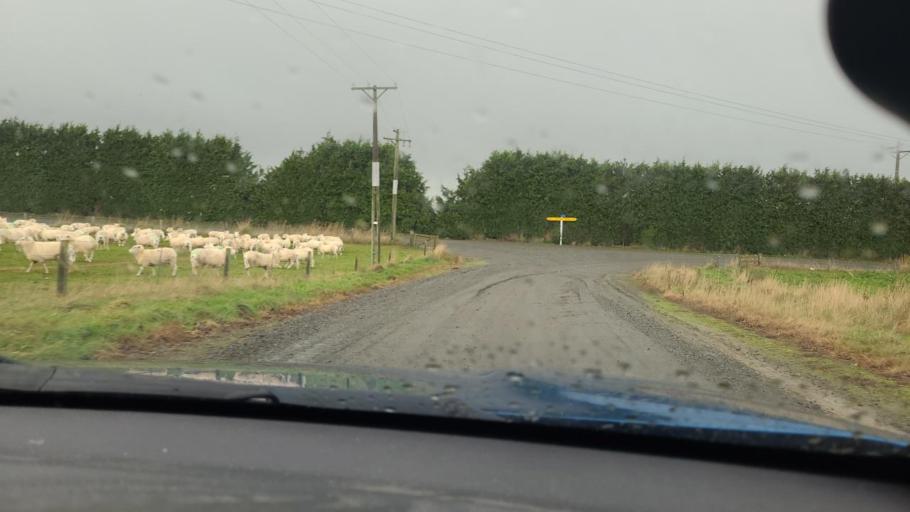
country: NZ
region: Southland
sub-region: Southland District
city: Winton
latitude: -46.0298
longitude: 168.0849
